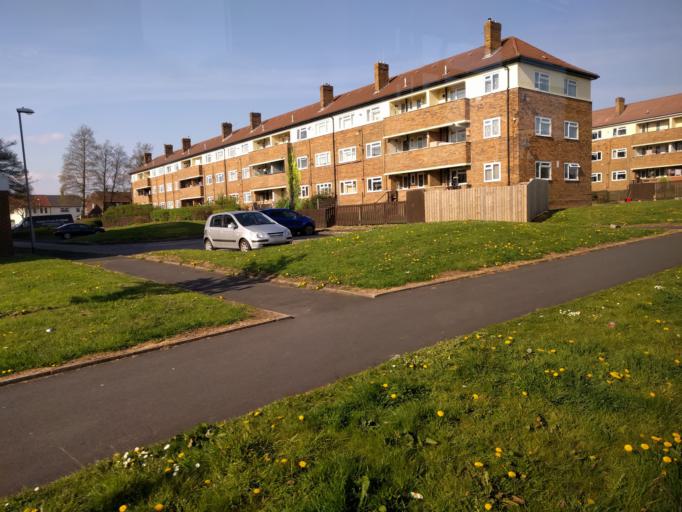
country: GB
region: England
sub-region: Manchester
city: Ringway
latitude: 53.3921
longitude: -2.2875
